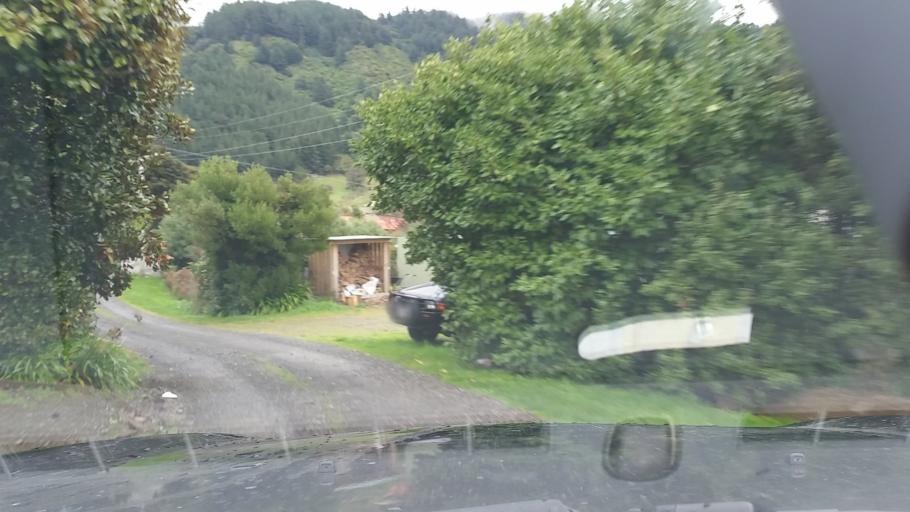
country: NZ
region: Marlborough
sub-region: Marlborough District
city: Picton
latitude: -41.2701
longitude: 174.0772
